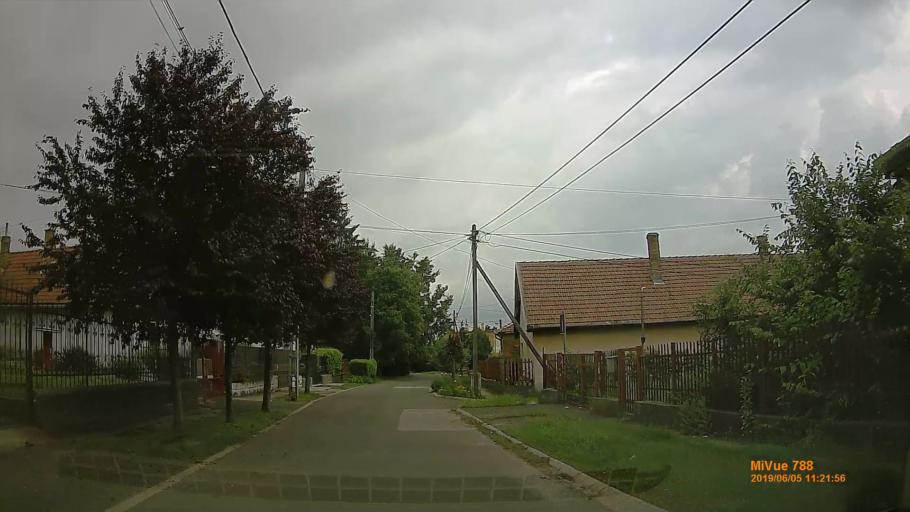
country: HU
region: Pest
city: Maglod
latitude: 47.4416
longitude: 19.3450
